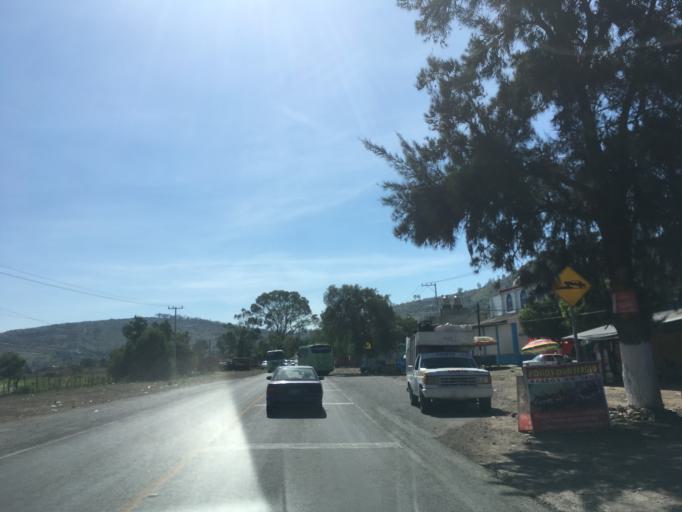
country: MX
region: Michoacan
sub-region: Morelia
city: Puerto de Buenavista (Lazaro Cardenas)
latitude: 19.6884
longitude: -101.1167
